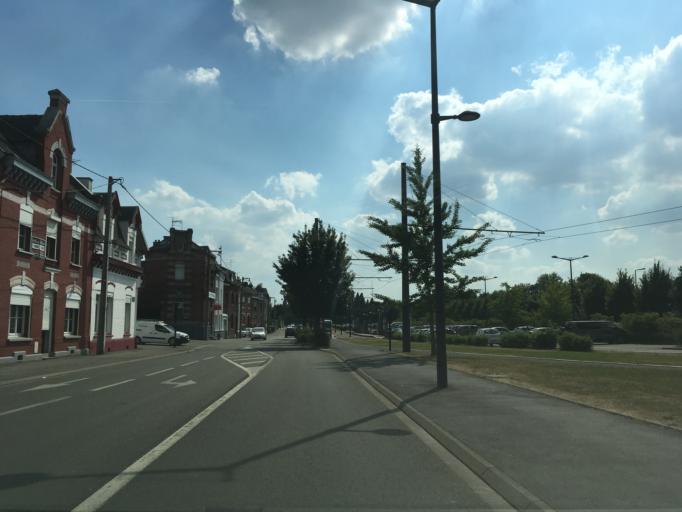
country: FR
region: Nord-Pas-de-Calais
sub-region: Departement du Nord
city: Valenciennes
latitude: 50.3494
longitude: 3.5205
